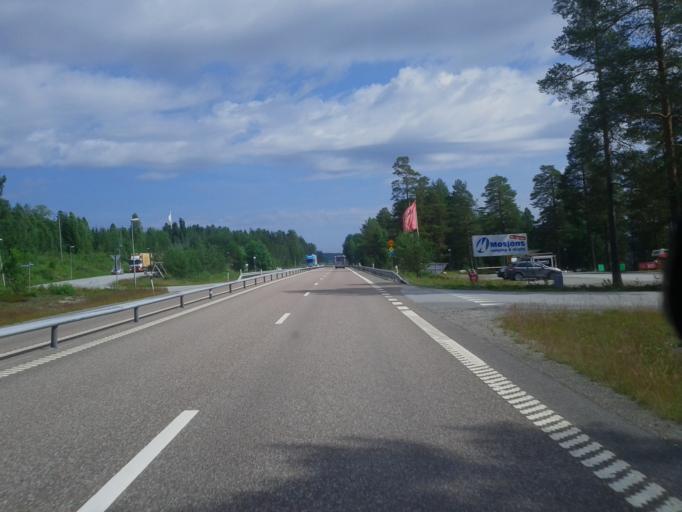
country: SE
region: Vaesternorrland
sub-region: OErnskoeldsviks Kommun
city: Husum
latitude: 63.3171
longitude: 19.0129
